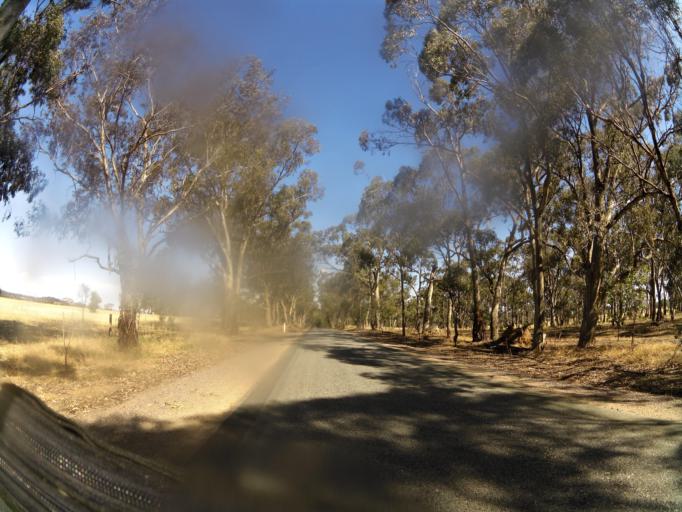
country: AU
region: Victoria
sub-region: Campaspe
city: Kyabram
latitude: -36.8784
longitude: 145.0874
